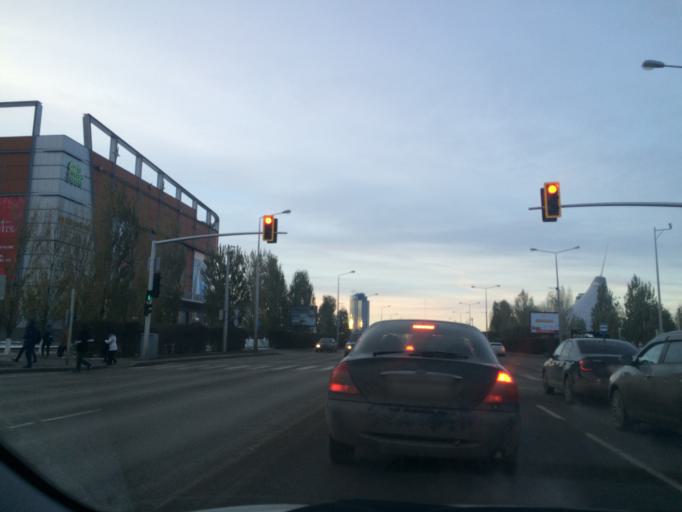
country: KZ
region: Astana Qalasy
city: Astana
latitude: 51.1398
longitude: 71.4096
